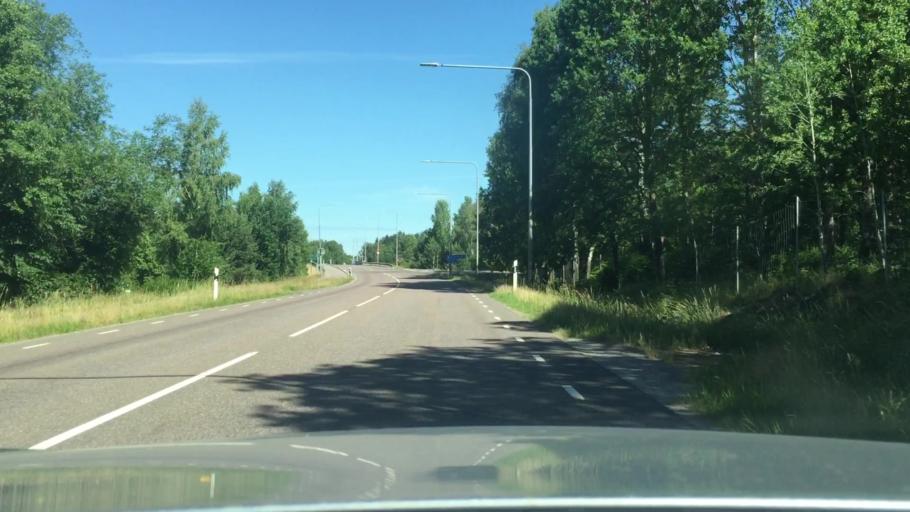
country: SE
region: Vaestra Goetaland
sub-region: Mariestads Kommun
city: Mariestad
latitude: 58.6824
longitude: 13.8463
